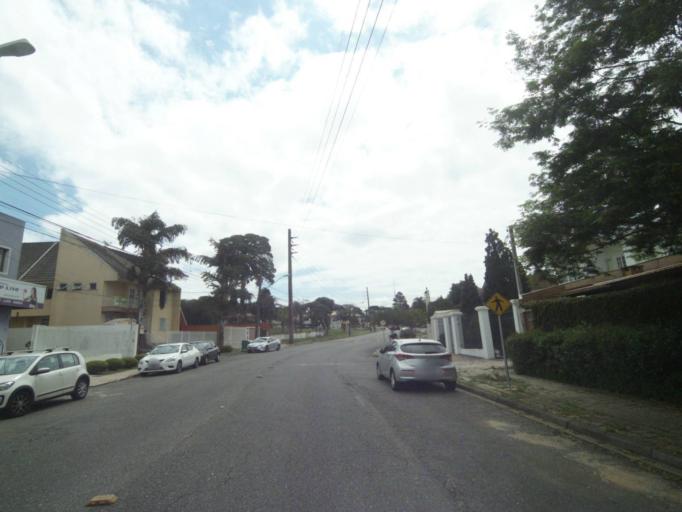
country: BR
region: Parana
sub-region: Curitiba
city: Curitiba
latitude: -25.4019
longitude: -49.2813
